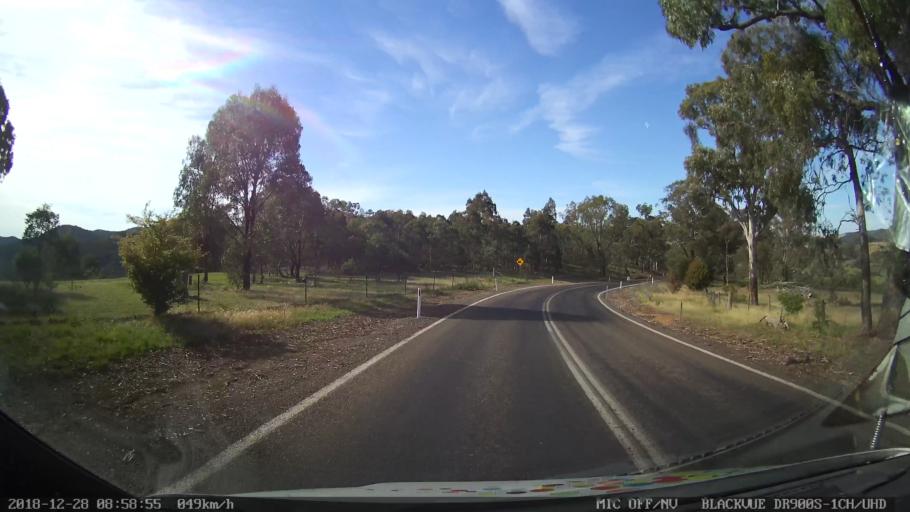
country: AU
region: New South Wales
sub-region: Upper Lachlan Shire
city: Crookwell
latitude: -34.1305
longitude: 149.3329
